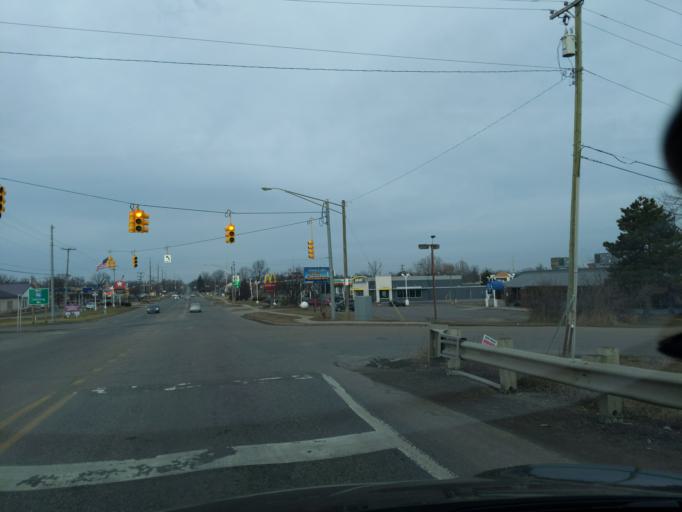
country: US
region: Michigan
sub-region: Livingston County
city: Fowlerville
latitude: 42.6476
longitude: -84.0726
